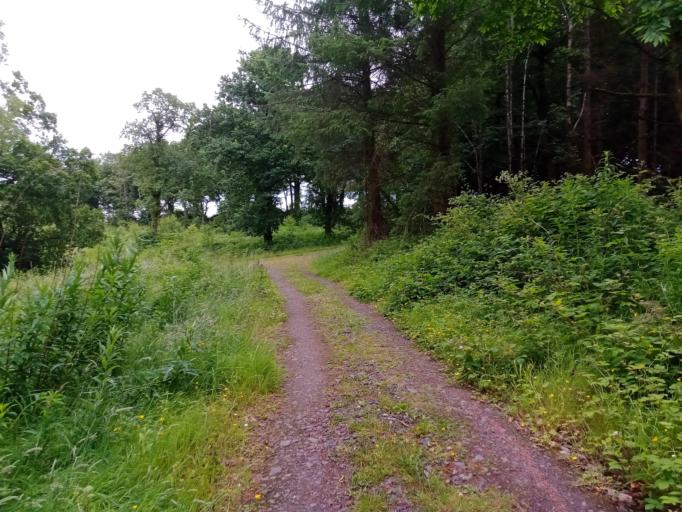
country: IE
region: Leinster
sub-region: Kilkenny
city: Piltown
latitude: 52.4497
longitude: -7.2708
